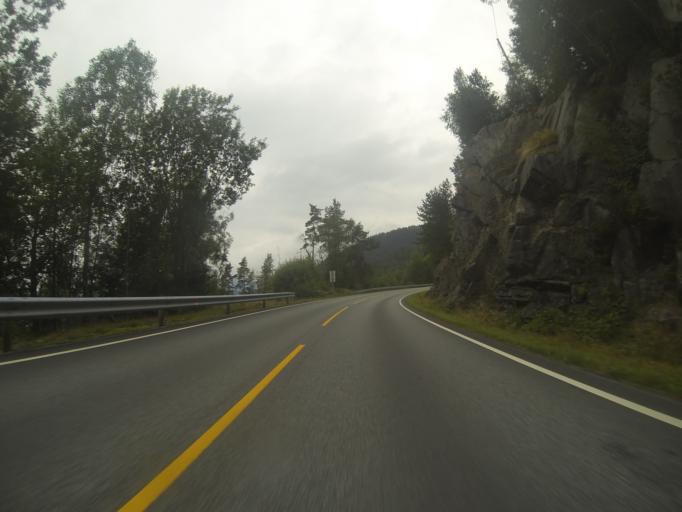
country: NO
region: Rogaland
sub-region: Suldal
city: Sand
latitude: 59.4808
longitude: 6.1994
